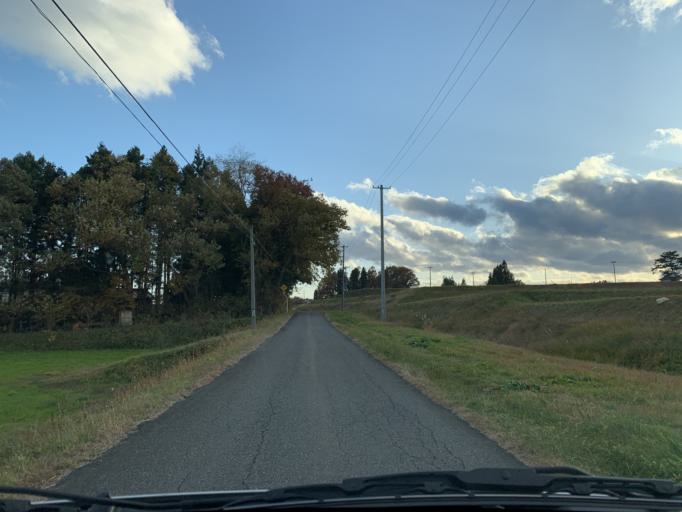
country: JP
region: Iwate
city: Mizusawa
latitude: 39.1045
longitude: 141.0394
